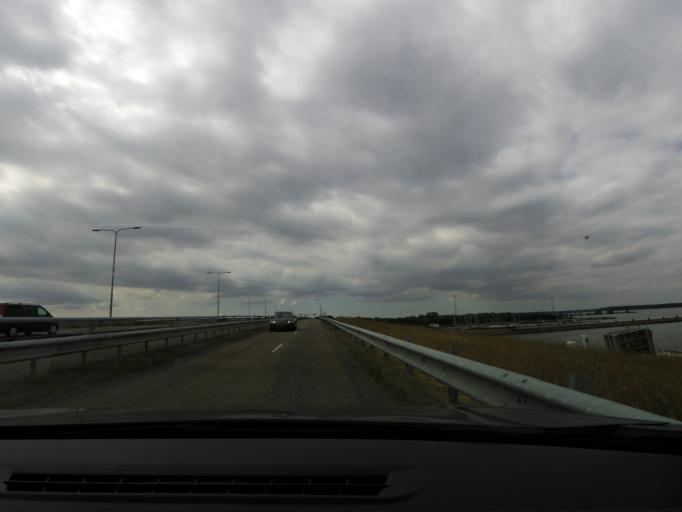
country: NL
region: North Brabant
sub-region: Gemeente Moerdijk
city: Willemstad
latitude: 51.6914
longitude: 4.4045
